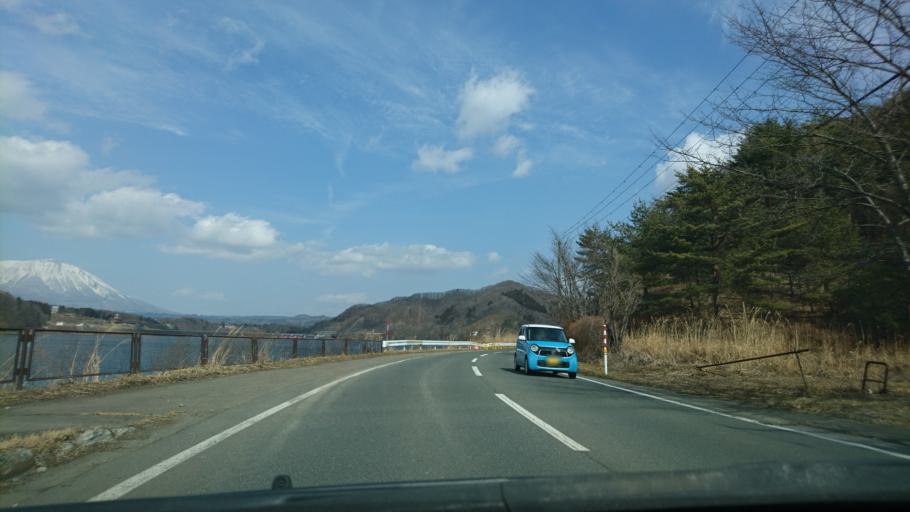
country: JP
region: Iwate
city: Shizukuishi
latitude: 39.6817
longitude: 141.0265
